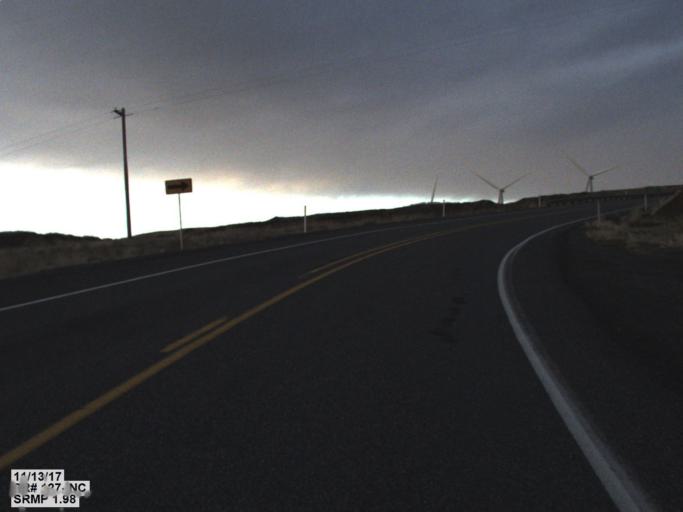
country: US
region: Washington
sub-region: Garfield County
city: Pomeroy
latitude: 46.5288
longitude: -117.7866
